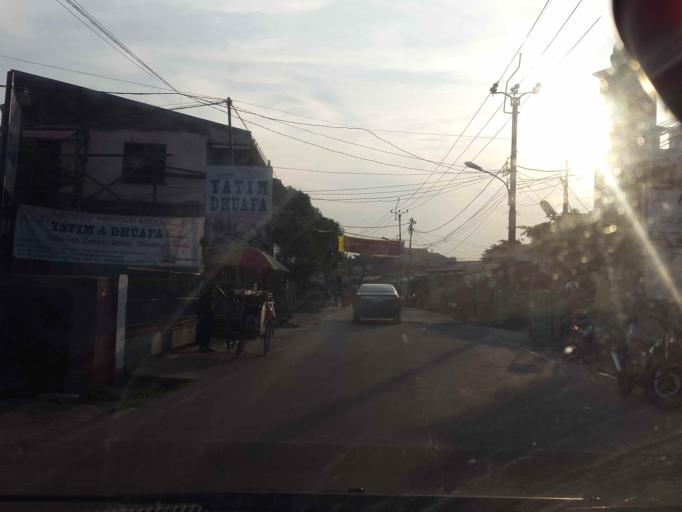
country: ID
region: Banten
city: South Tangerang
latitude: -6.2621
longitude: 106.7456
